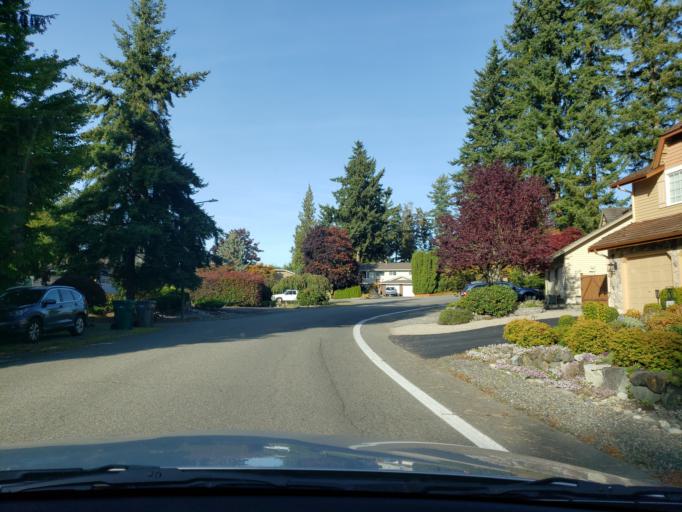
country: US
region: Washington
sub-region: Snohomish County
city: Meadowdale
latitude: 47.8706
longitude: -122.3196
